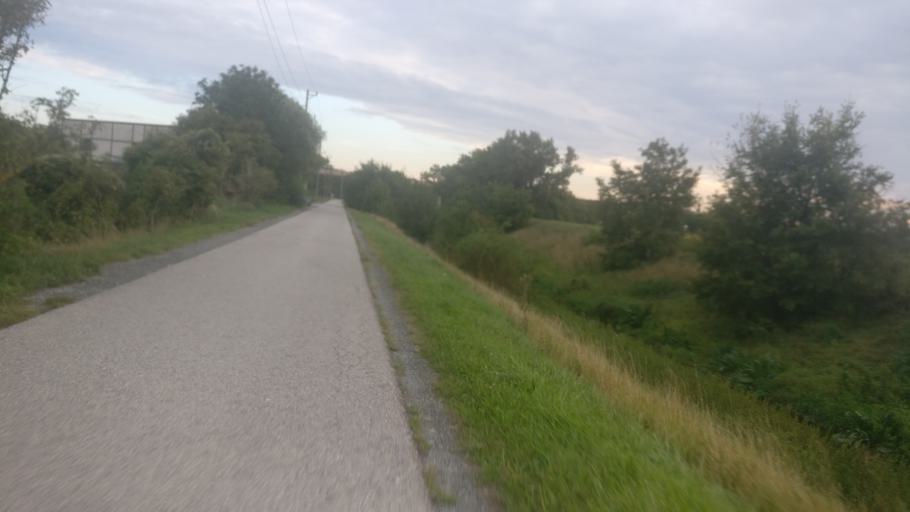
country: AT
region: Lower Austria
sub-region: Politischer Bezirk Wien-Umgebung
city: Lanzendorf
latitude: 48.0971
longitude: 16.4417
